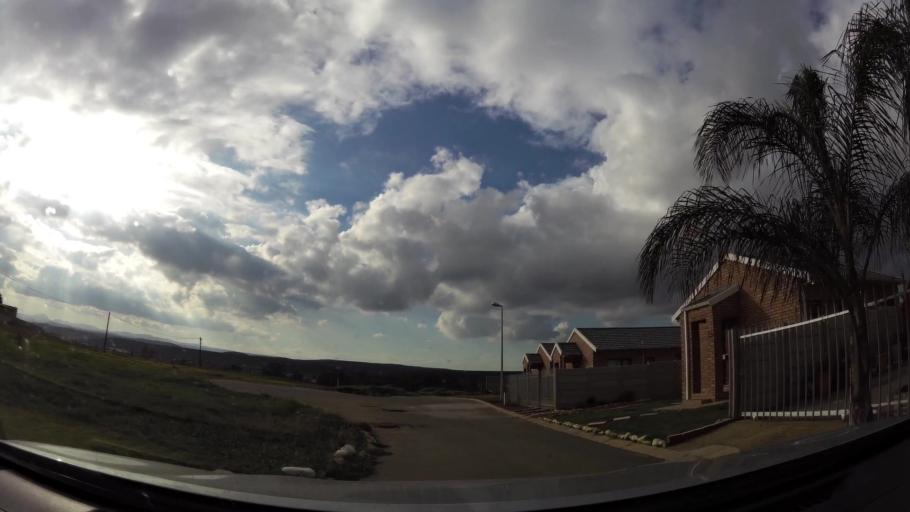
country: ZA
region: Eastern Cape
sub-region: Nelson Mandela Bay Metropolitan Municipality
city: Uitenhage
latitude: -33.7984
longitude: 25.4554
